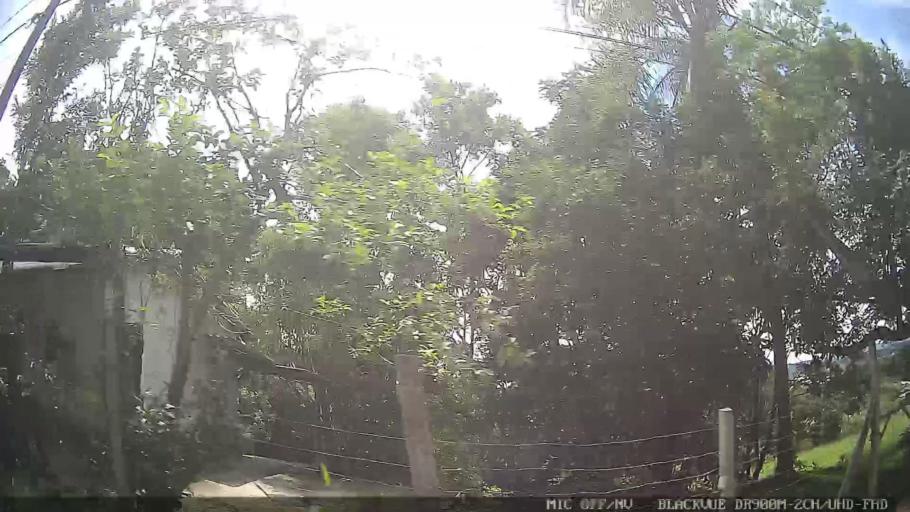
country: BR
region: Sao Paulo
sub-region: Santa Isabel
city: Santa Isabel
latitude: -23.3725
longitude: -46.1791
